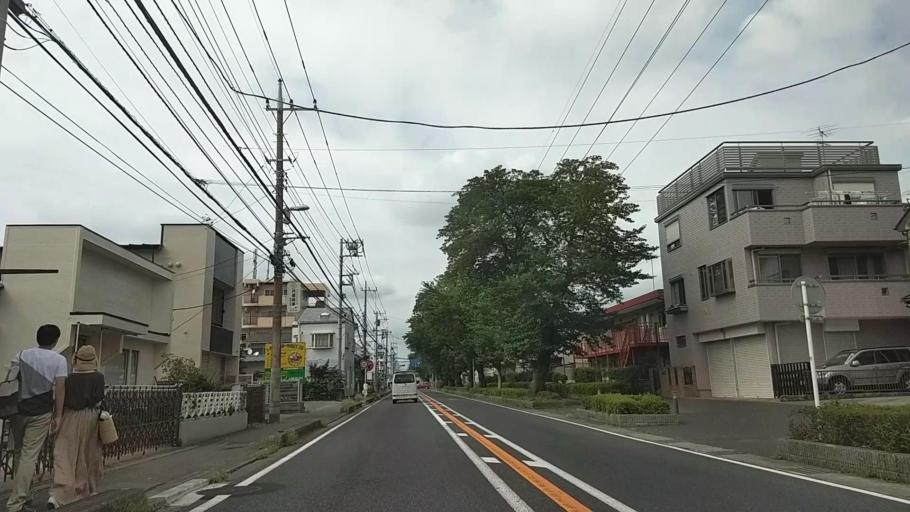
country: JP
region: Kanagawa
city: Minami-rinkan
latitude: 35.4467
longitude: 139.4674
